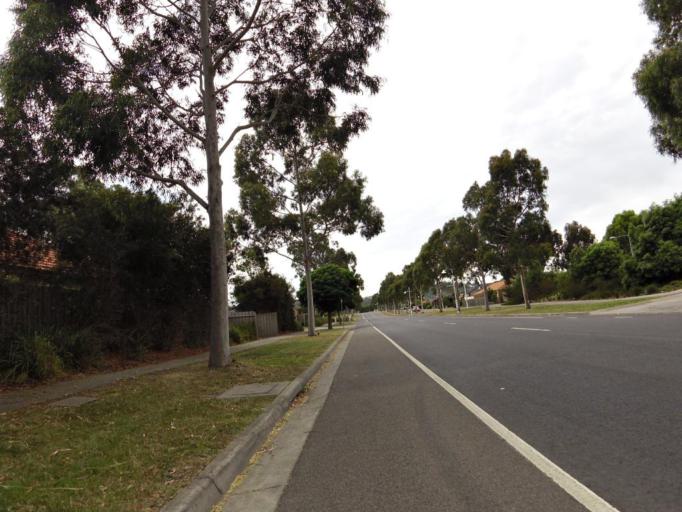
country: AU
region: Victoria
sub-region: Whittlesea
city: Mill Park
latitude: -37.6395
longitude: 145.0763
